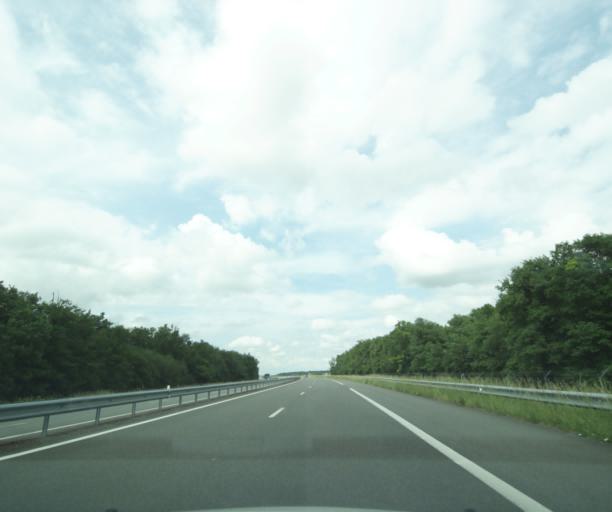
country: FR
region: Centre
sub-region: Departement du Cher
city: Levet
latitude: 46.8493
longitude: 2.4239
